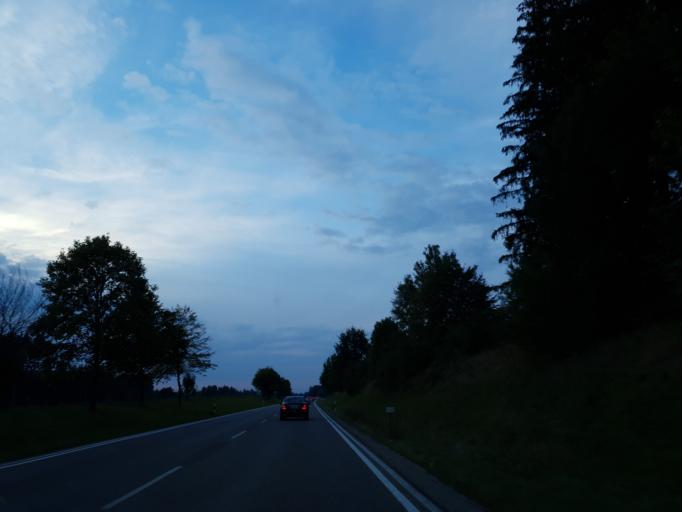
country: DE
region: Bavaria
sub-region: Swabia
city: Mauerstetten
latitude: 47.8558
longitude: 10.6617
